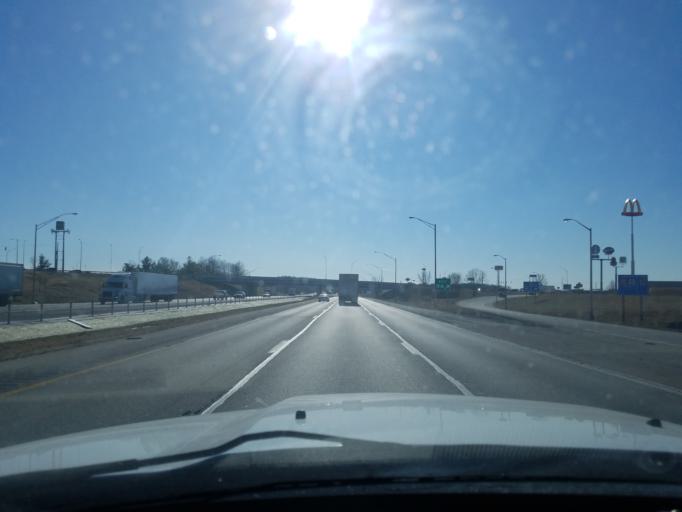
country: US
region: Kentucky
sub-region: Hardin County
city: Elizabethtown
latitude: 37.7162
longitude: -85.8294
